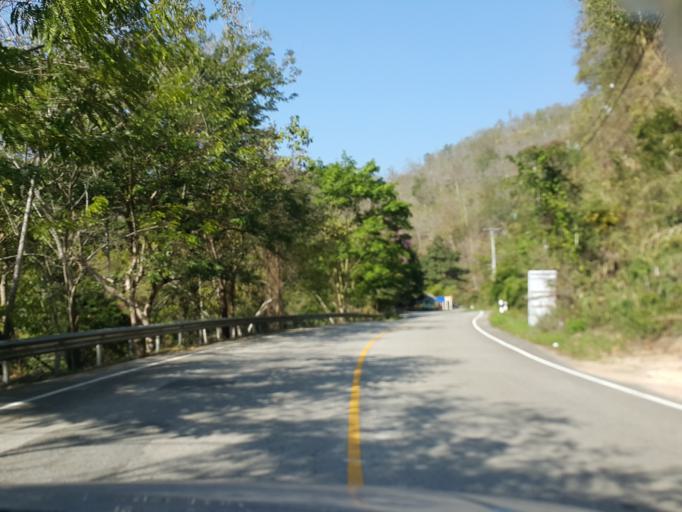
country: TH
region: Chiang Mai
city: Mae Wang
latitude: 18.6264
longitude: 98.7144
